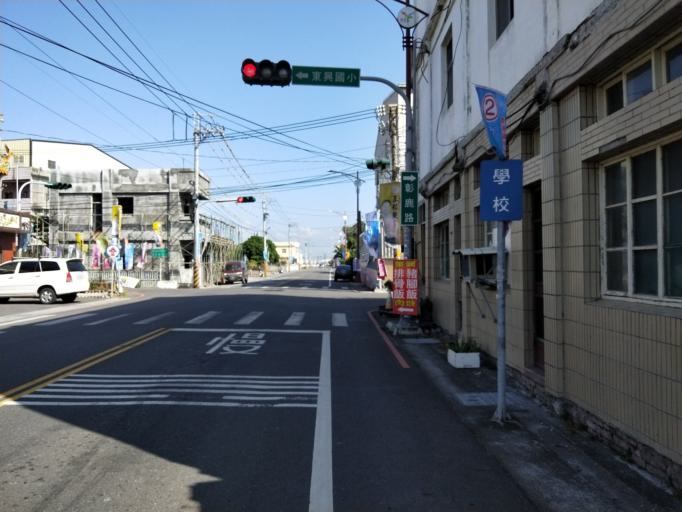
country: TW
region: Taiwan
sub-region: Changhua
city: Chang-hua
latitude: 24.0560
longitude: 120.4749
